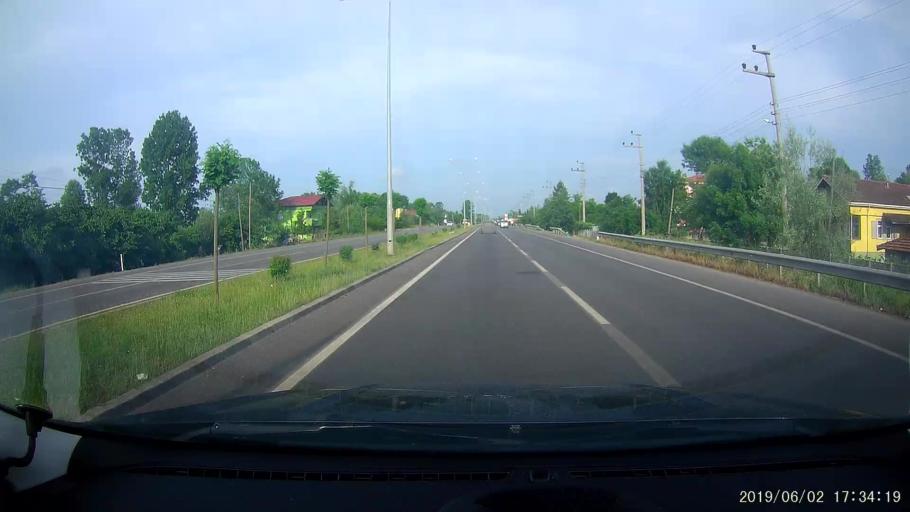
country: TR
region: Samsun
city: Terme
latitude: 41.2203
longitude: 36.8666
